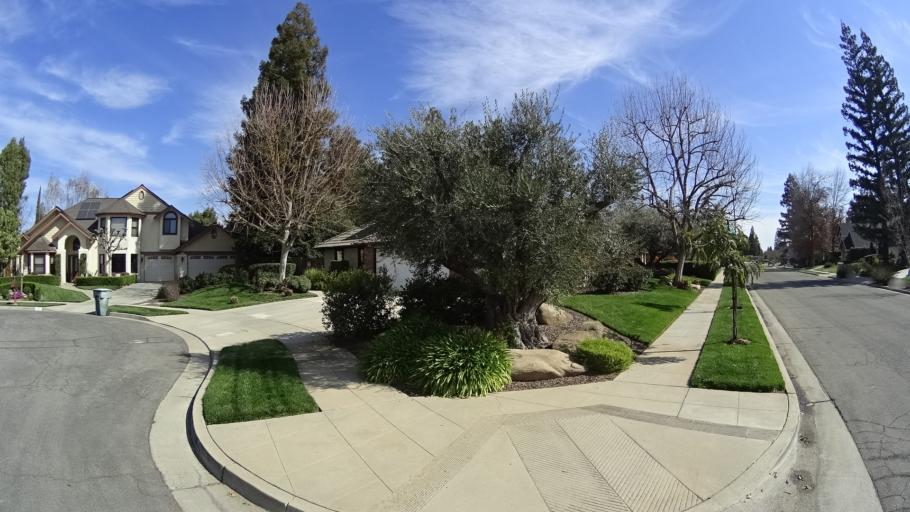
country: US
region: California
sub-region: Fresno County
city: Clovis
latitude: 36.8641
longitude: -119.7640
